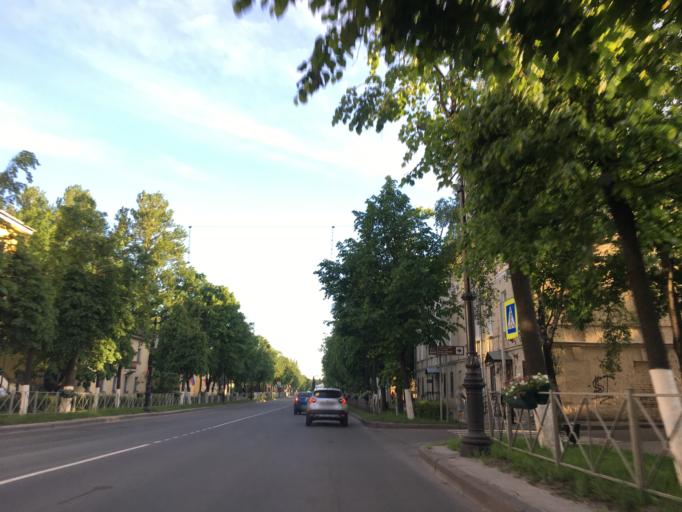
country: RU
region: Leningrad
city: Gatchina
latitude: 59.5703
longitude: 30.1233
